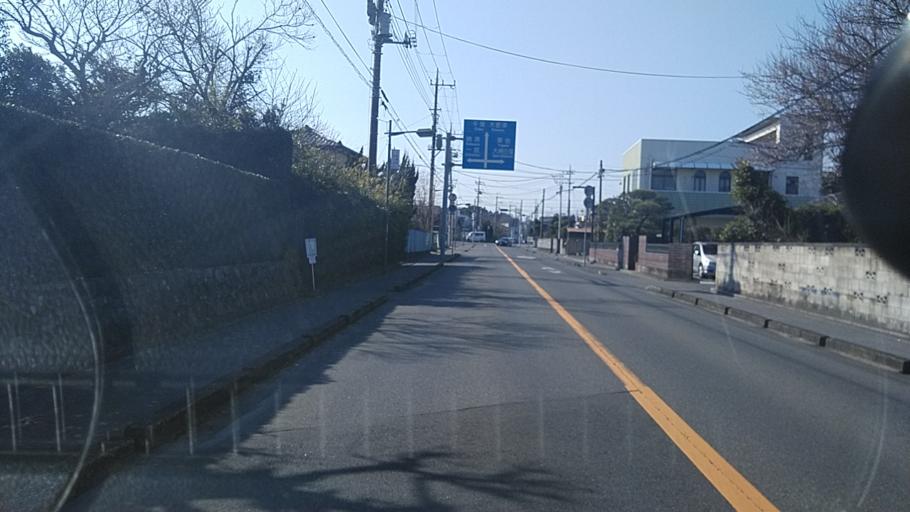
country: JP
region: Chiba
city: Mobara
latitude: 35.4303
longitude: 140.2951
